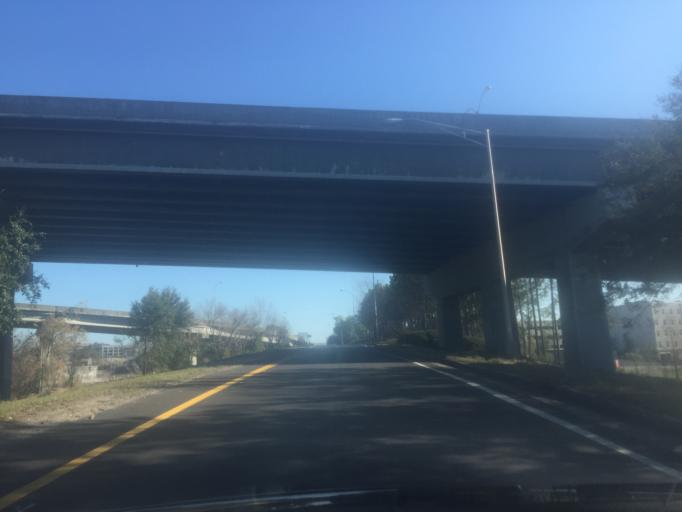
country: US
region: Georgia
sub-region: Chatham County
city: Savannah
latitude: 32.0816
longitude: -81.1054
